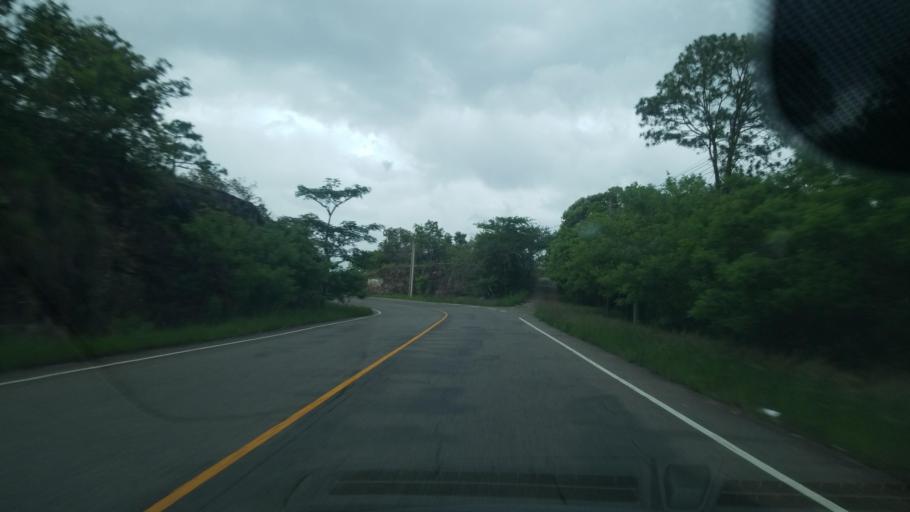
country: HN
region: Ocotepeque
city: Sinuapa
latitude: 14.5229
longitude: -89.2454
